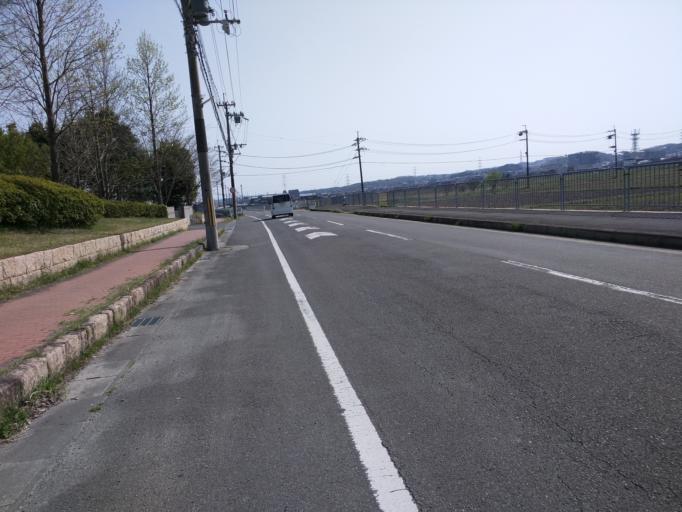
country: JP
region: Kyoto
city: Tanabe
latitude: 34.7731
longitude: 135.7975
